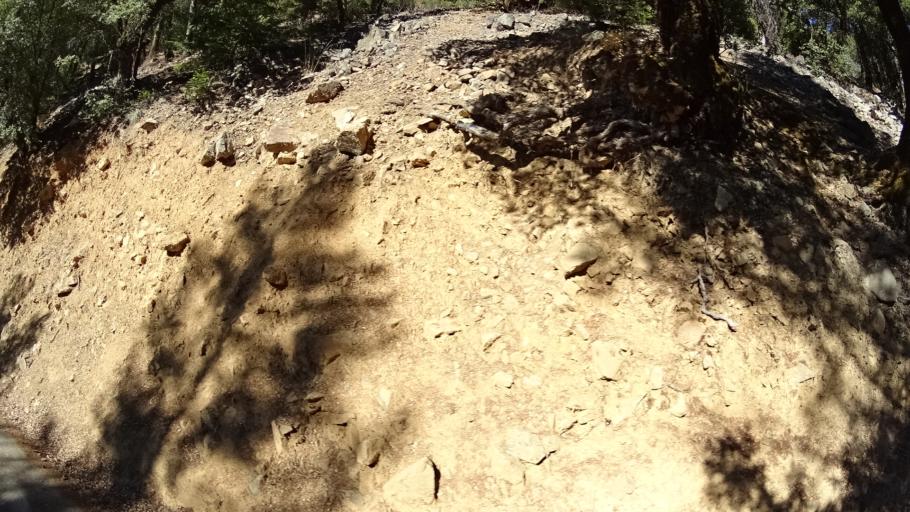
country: US
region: California
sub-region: Siskiyou County
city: Happy Camp
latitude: 41.2957
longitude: -123.1079
